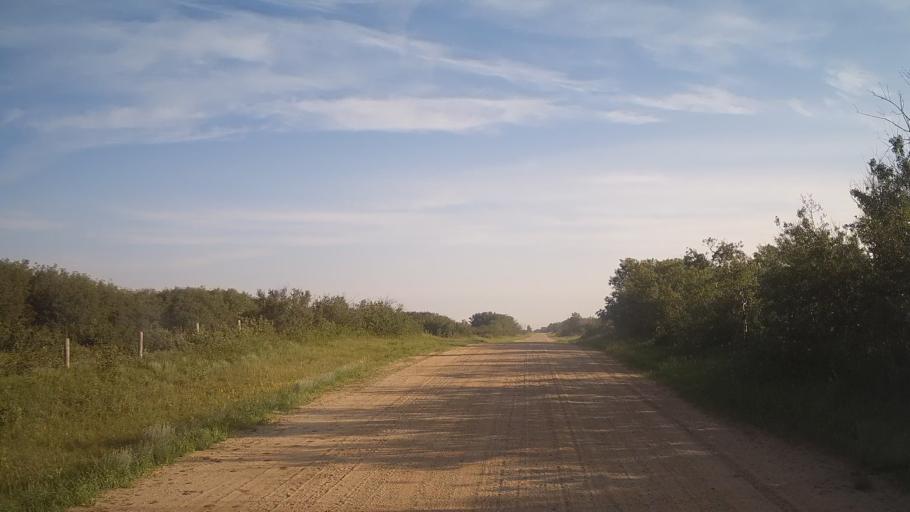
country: CA
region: Saskatchewan
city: Saskatoon
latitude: 51.8394
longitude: -106.5240
